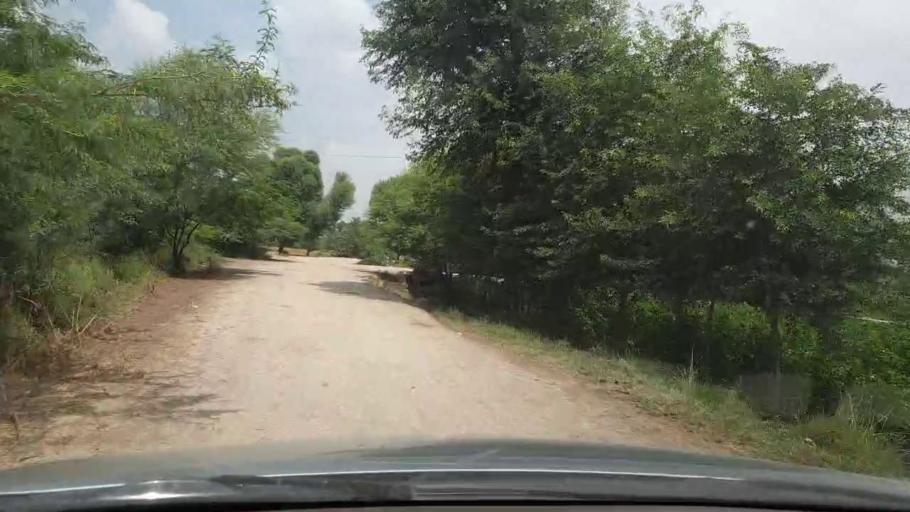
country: PK
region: Sindh
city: Kot Diji
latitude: 27.4181
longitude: 68.7579
